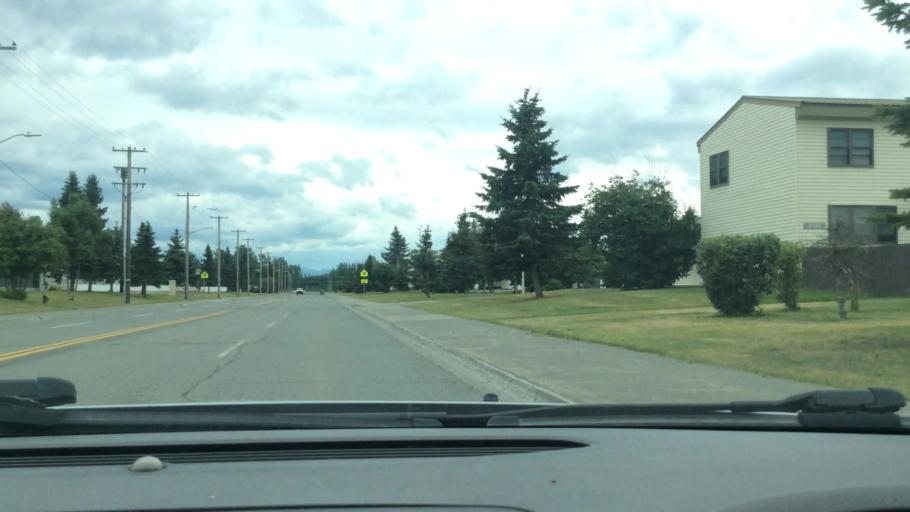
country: US
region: Alaska
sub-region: Anchorage Municipality
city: Anchorage
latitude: 61.2341
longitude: -149.8493
